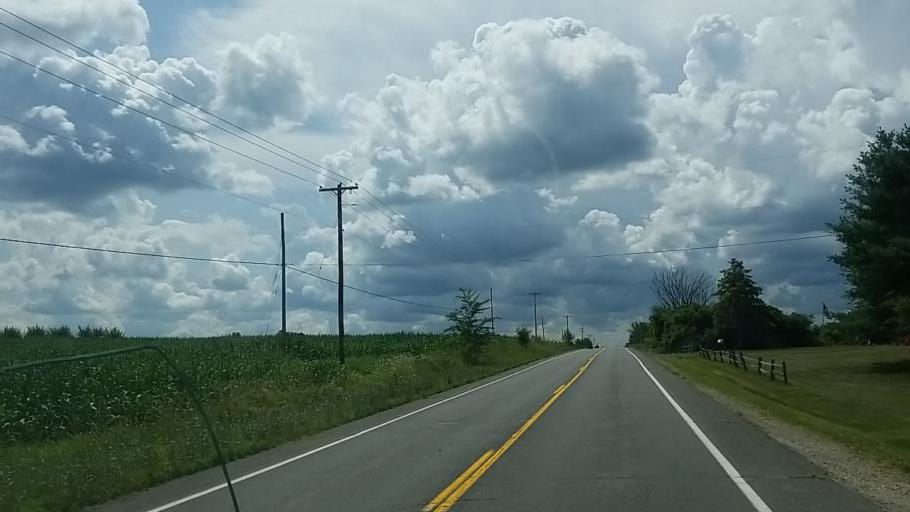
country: US
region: Michigan
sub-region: Kent County
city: Sparta
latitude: 43.0933
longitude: -85.7682
